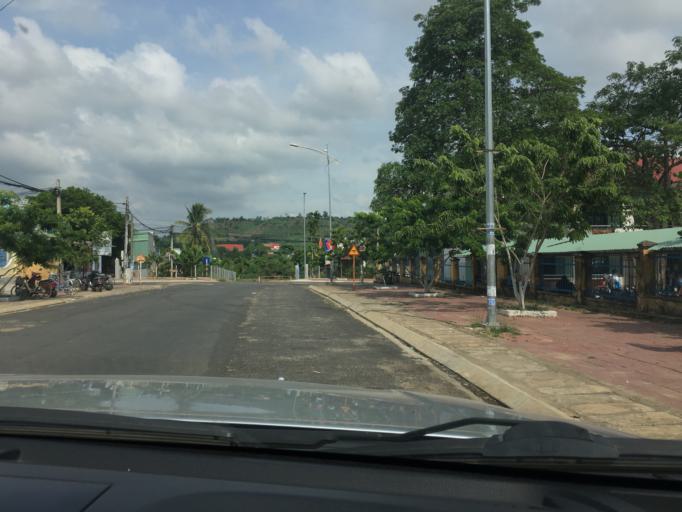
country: VN
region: Gia Lai
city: Kong Chro
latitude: 13.7749
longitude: 108.5227
